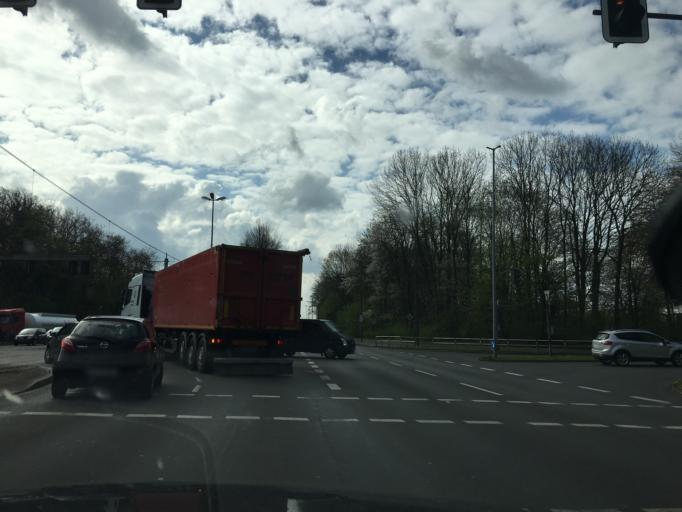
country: DE
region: North Rhine-Westphalia
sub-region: Regierungsbezirk Munster
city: Gladbeck
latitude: 51.5643
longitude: 7.0588
